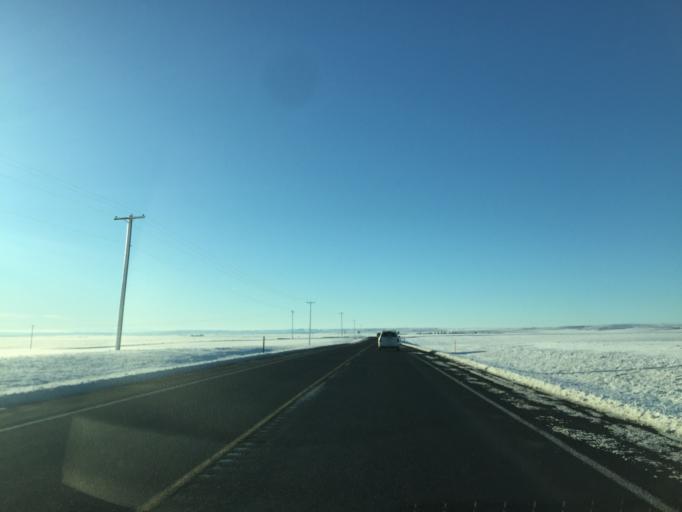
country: US
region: Washington
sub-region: Okanogan County
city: Coulee Dam
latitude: 47.6845
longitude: -119.0375
